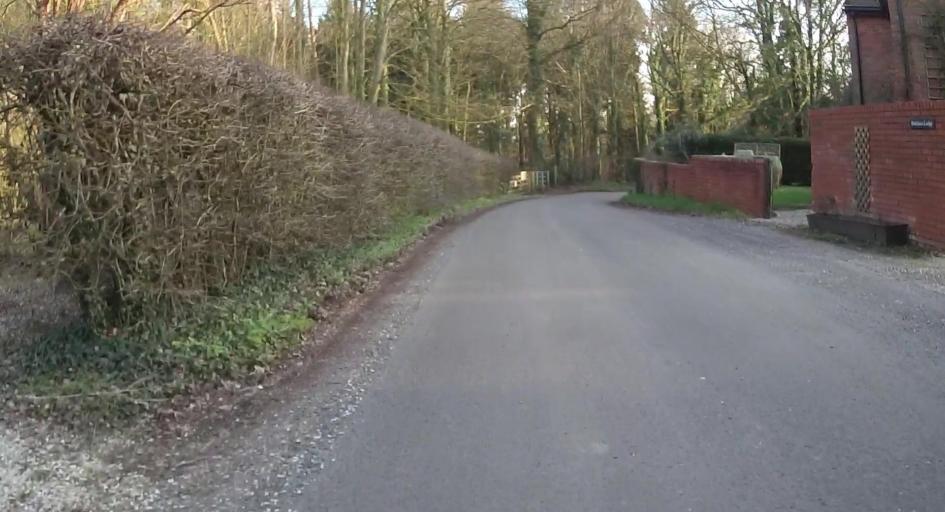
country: GB
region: England
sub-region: Hampshire
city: Four Marks
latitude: 51.1758
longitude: -1.0633
